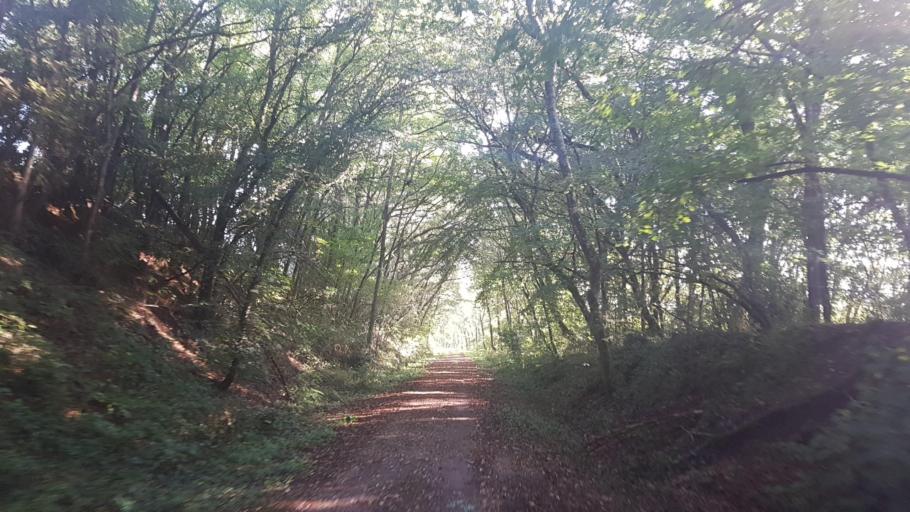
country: FR
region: Poitou-Charentes
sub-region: Departement de la Vienne
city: Saint-Savin
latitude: 46.5736
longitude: 0.8681
